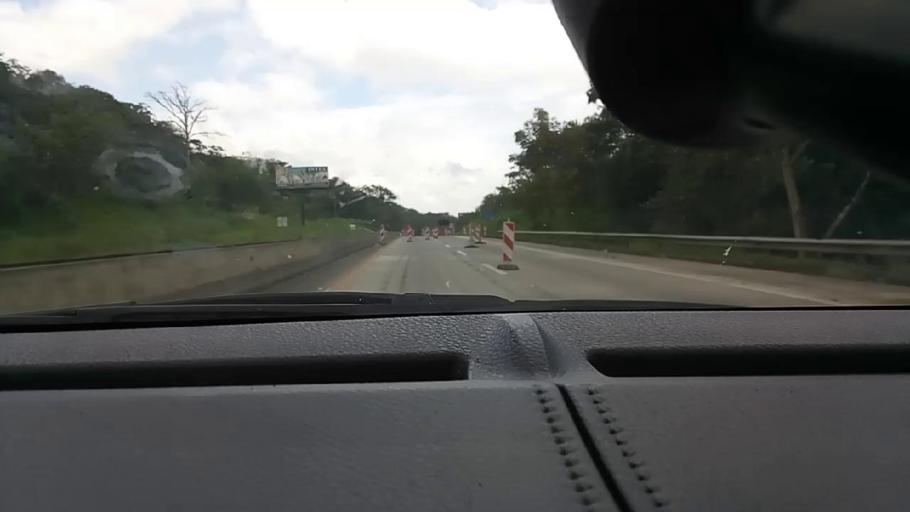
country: PA
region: Panama
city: Chilibre
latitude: 9.1605
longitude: -79.6382
